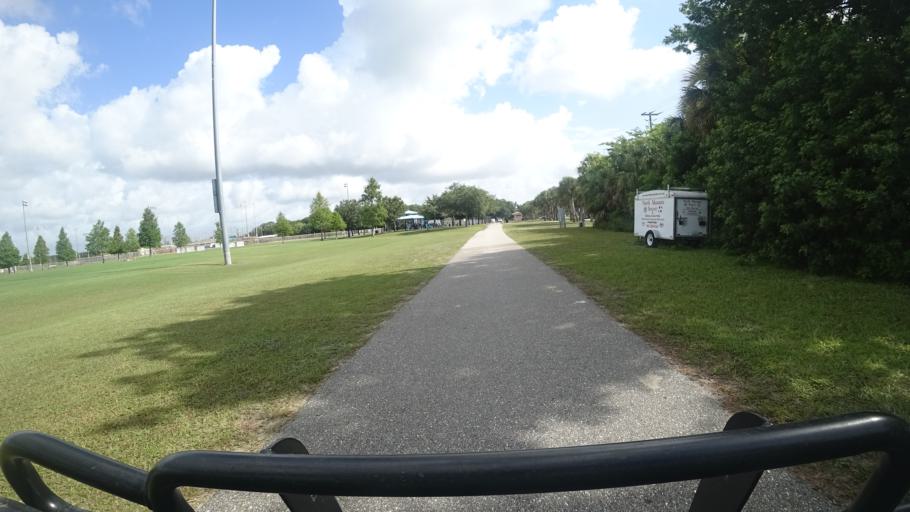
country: US
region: Florida
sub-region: Manatee County
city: Ellenton
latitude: 27.5751
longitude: -82.4842
